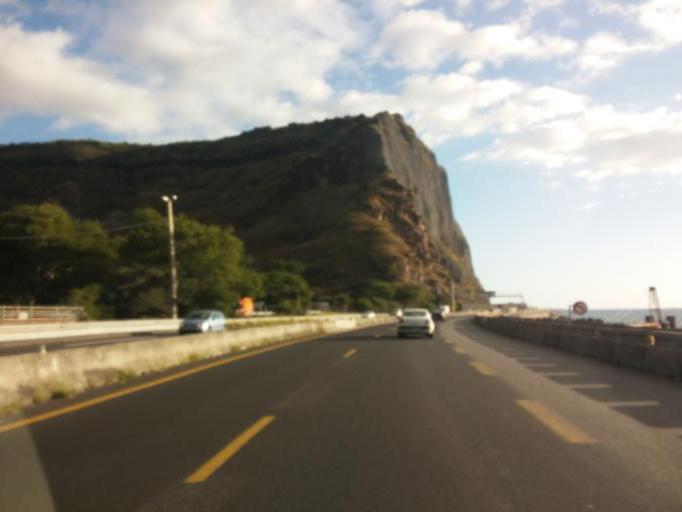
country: RE
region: Reunion
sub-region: Reunion
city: La Possession
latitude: -20.8962
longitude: 55.3762
